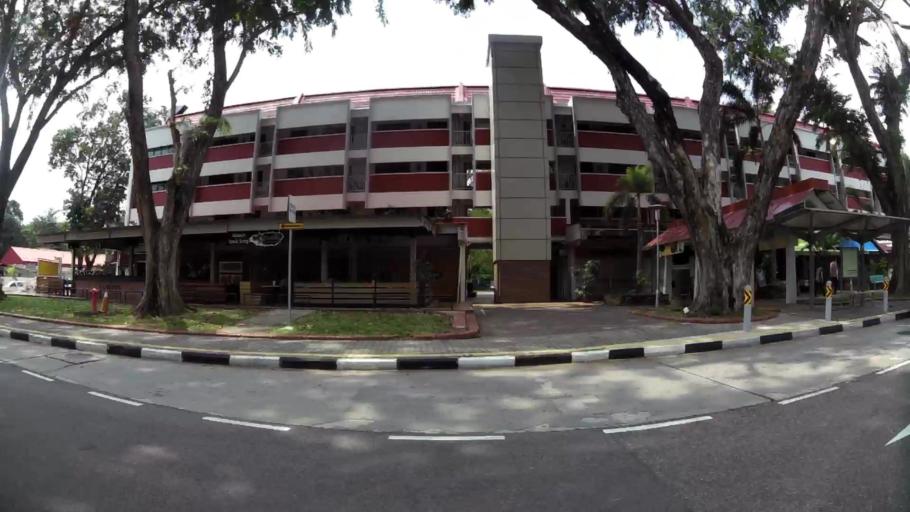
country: MY
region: Johor
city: Kampung Pasir Gudang Baru
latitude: 1.3889
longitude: 103.9871
